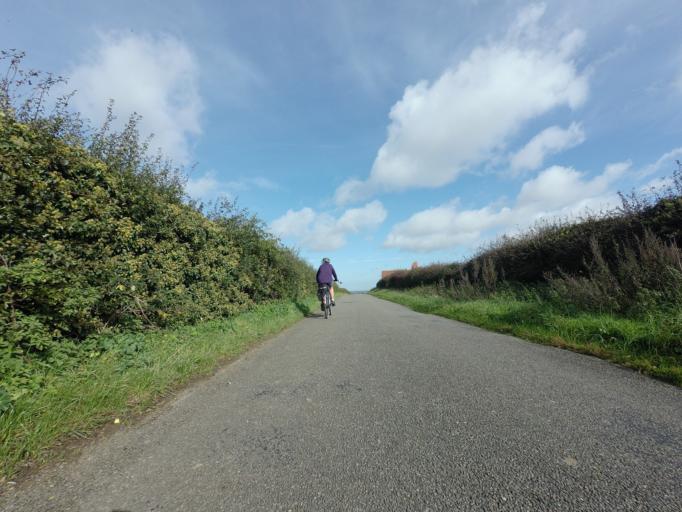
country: GB
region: England
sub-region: Norfolk
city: Wells-next-the-Sea
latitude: 52.9332
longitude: 0.7264
